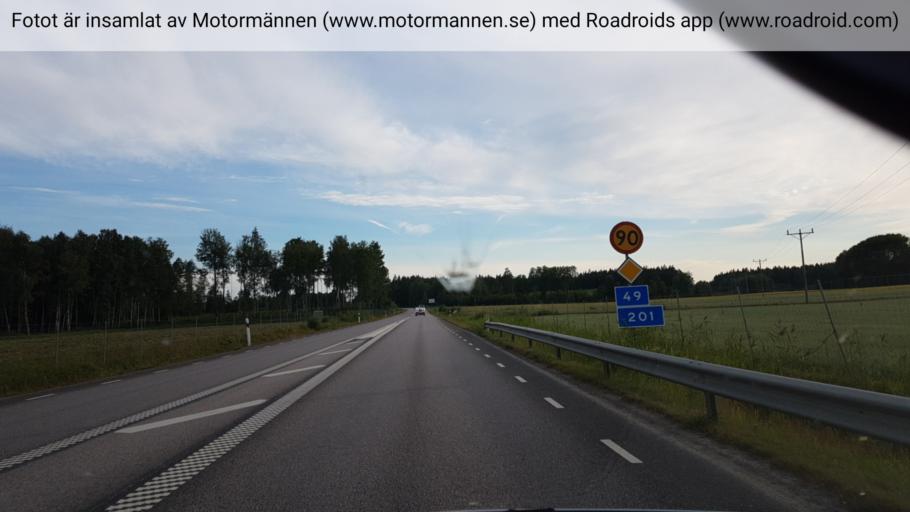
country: SE
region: Vaestra Goetaland
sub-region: Tibro Kommun
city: Tibro
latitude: 58.4422
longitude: 14.1823
